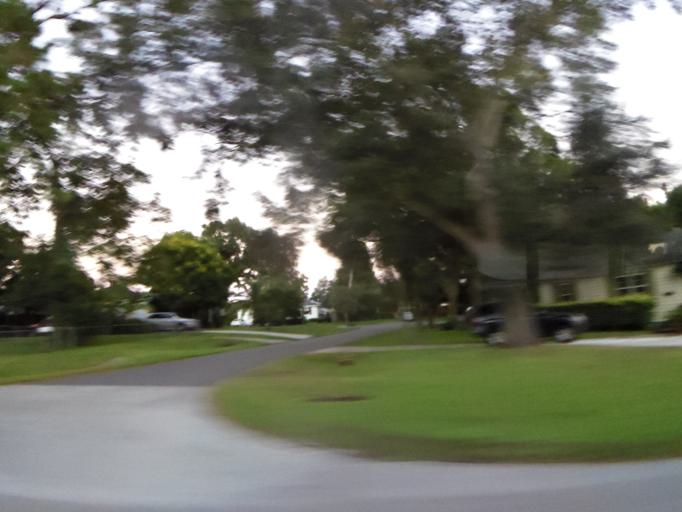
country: US
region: Florida
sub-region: Duval County
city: Jacksonville
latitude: 30.3009
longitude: -81.7220
